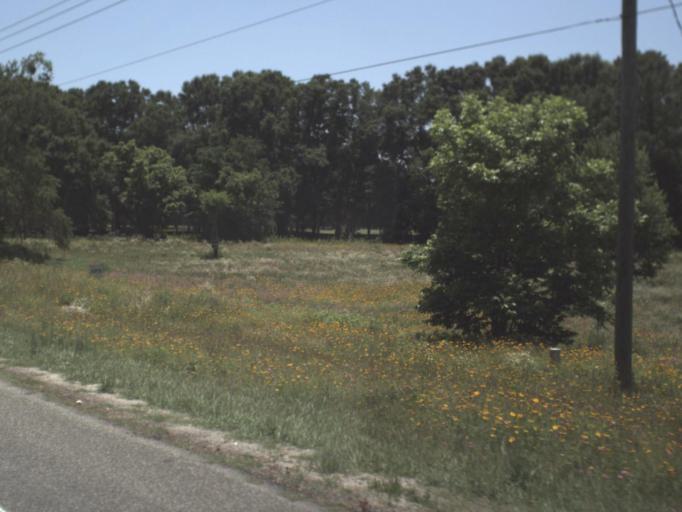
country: US
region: Florida
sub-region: Suwannee County
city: Live Oak
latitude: 30.2633
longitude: -82.9144
